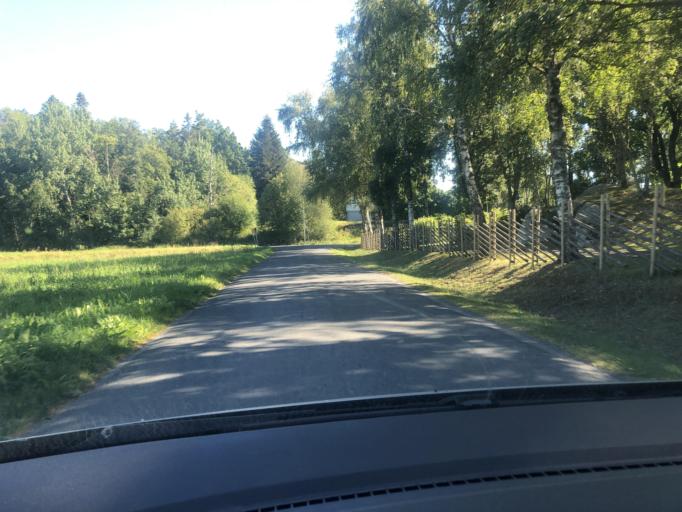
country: SE
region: Joenkoeping
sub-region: Jonkopings Kommun
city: Huskvarna
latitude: 57.7970
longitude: 14.3134
